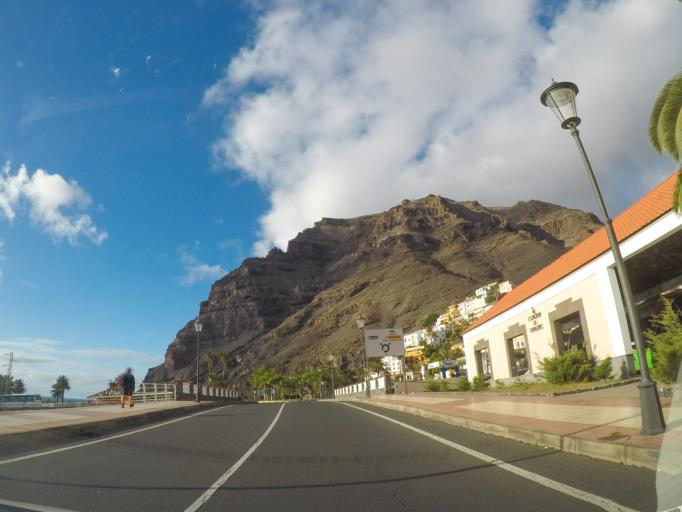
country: ES
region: Canary Islands
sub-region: Provincia de Santa Cruz de Tenerife
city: Alajero
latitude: 28.0936
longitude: -17.3354
